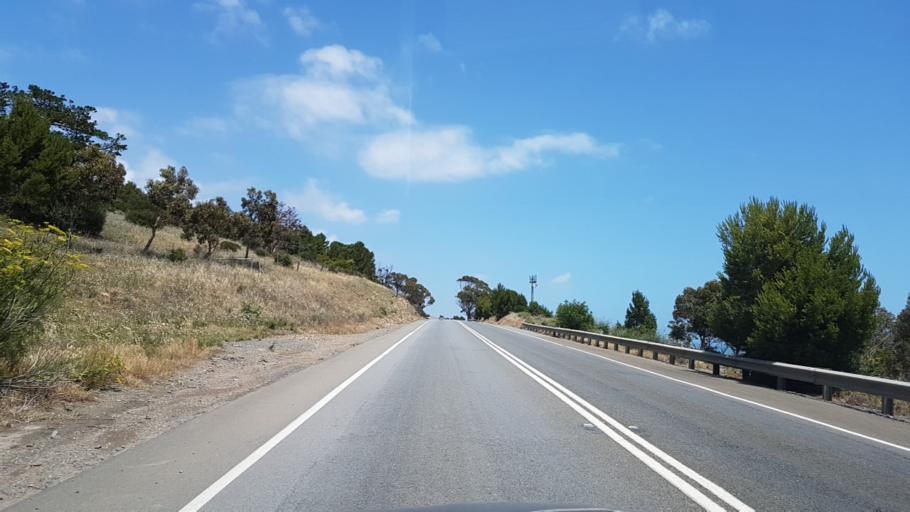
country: AU
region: South Australia
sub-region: Onkaparinga
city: Aldinga
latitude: -35.3372
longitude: 138.4664
